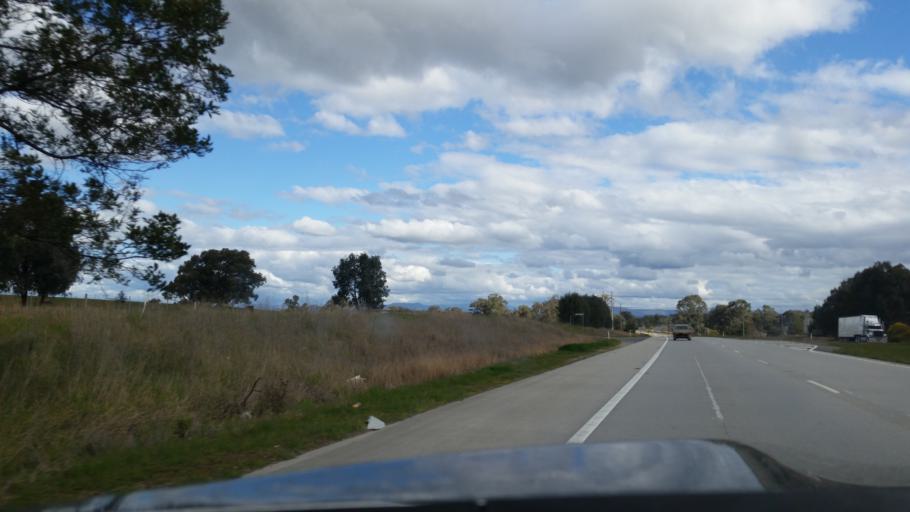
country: AU
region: New South Wales
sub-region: Albury Municipality
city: Lavington
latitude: -35.9925
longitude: 146.9948
